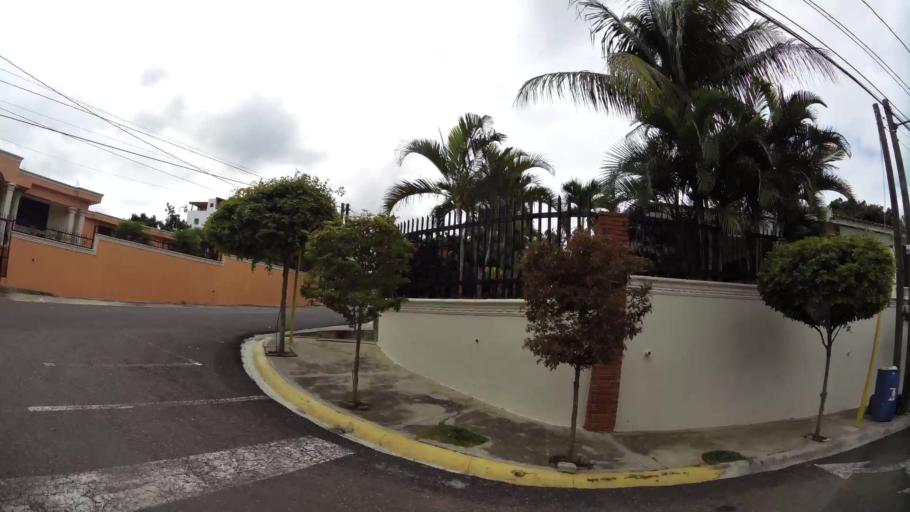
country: DO
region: Santiago
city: Santiago de los Caballeros
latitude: 19.4338
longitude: -70.6618
